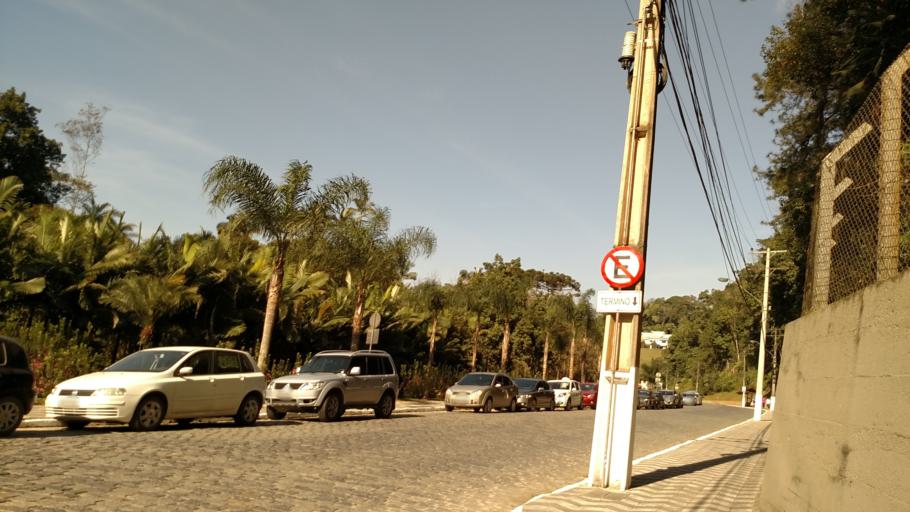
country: BR
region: Santa Catarina
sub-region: Pomerode
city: Pomerode
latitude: -26.7291
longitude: -49.0678
